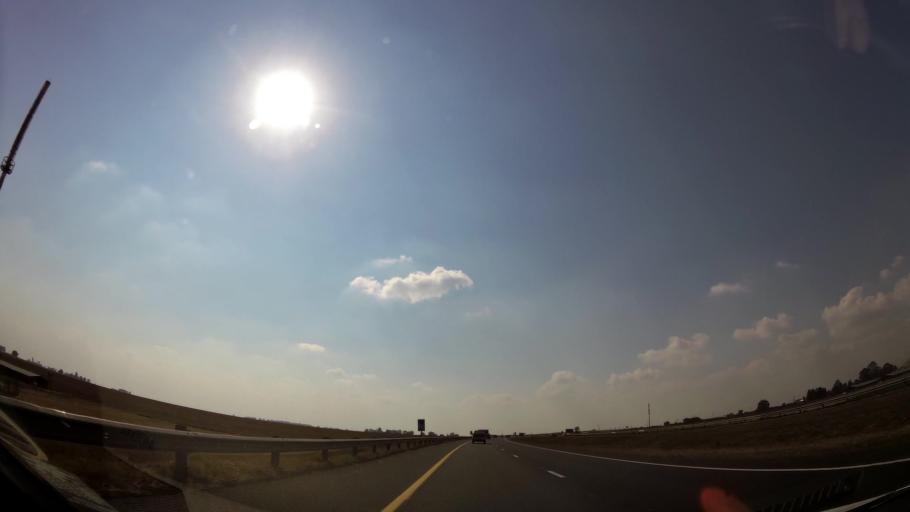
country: ZA
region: Mpumalanga
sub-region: Nkangala District Municipality
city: Delmas
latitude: -26.1518
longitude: 28.5270
